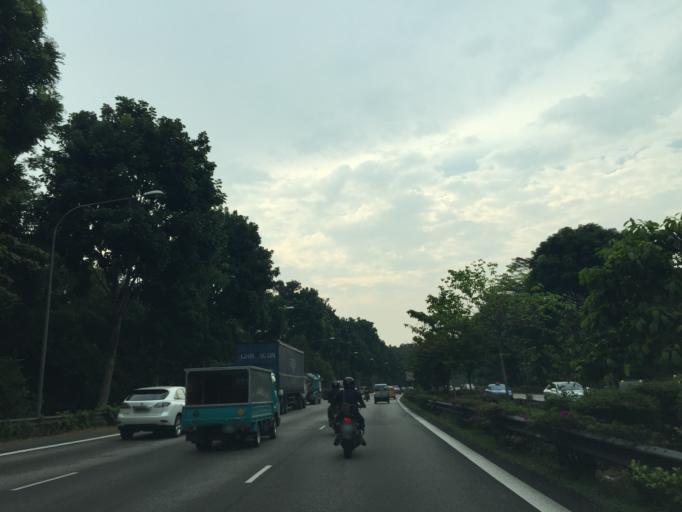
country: SG
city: Singapore
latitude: 1.3572
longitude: 103.7830
